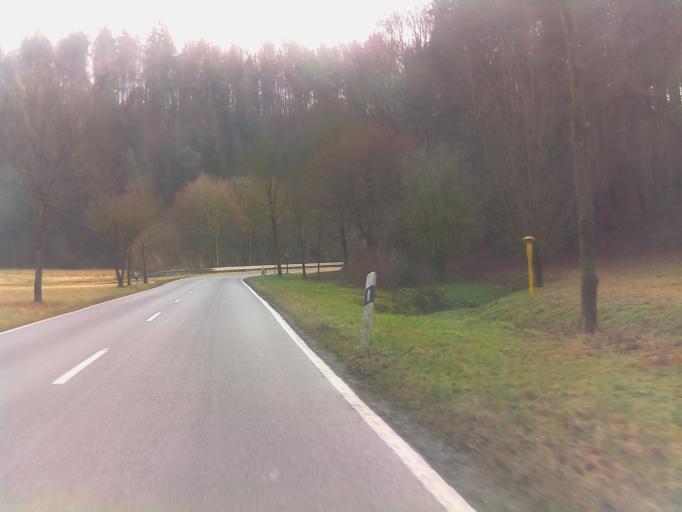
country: DE
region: Thuringia
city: Utendorf
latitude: 50.5992
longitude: 10.4425
